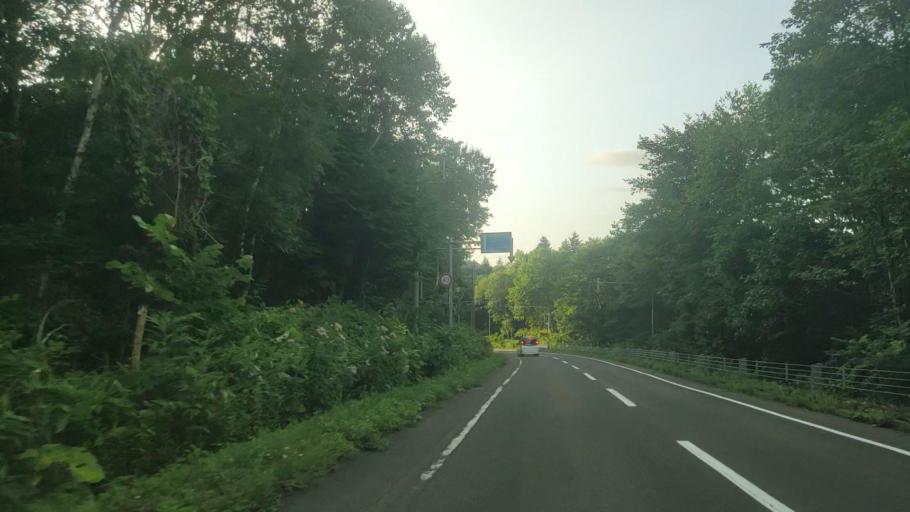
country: JP
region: Hokkaido
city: Bibai
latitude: 43.1770
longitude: 142.0697
